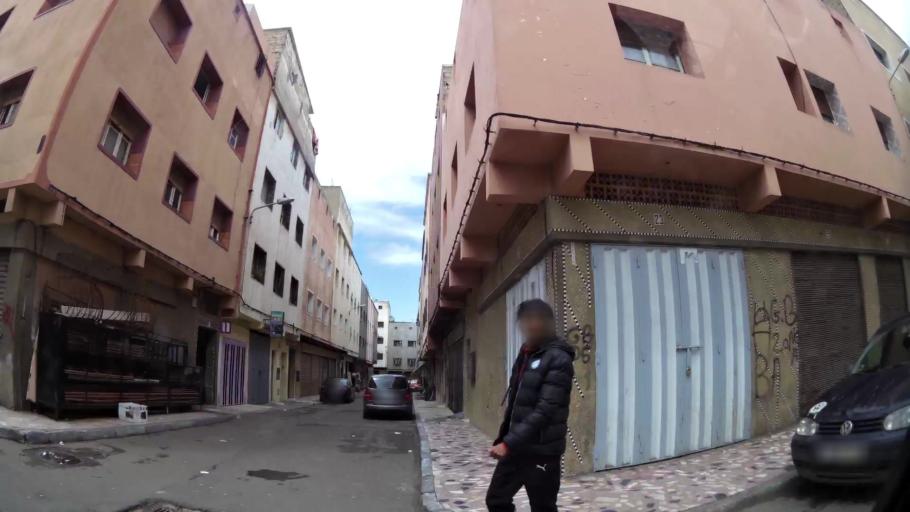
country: MA
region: Grand Casablanca
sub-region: Mediouna
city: Tit Mellil
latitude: 33.6110
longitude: -7.5118
